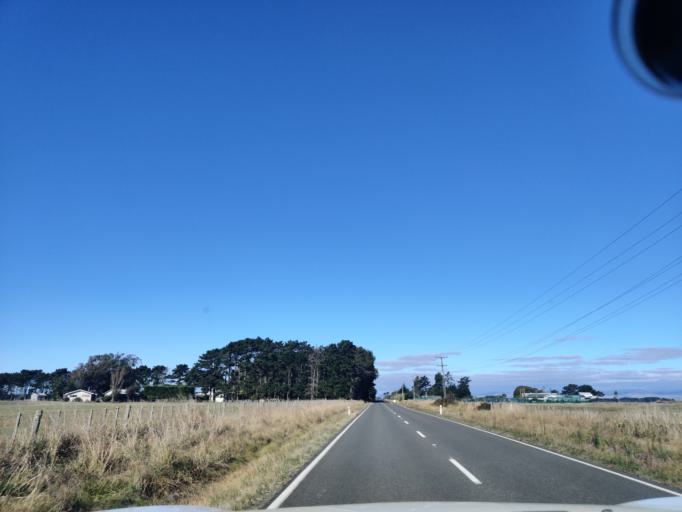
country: NZ
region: Manawatu-Wanganui
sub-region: Horowhenua District
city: Foxton
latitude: -40.3862
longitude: 175.2884
